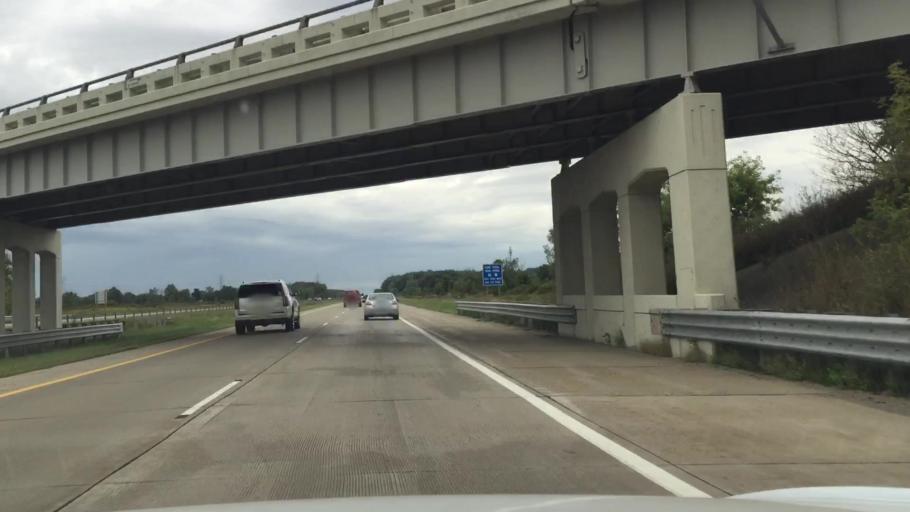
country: US
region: Michigan
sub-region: Macomb County
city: Richmond
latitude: 42.7804
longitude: -82.6732
